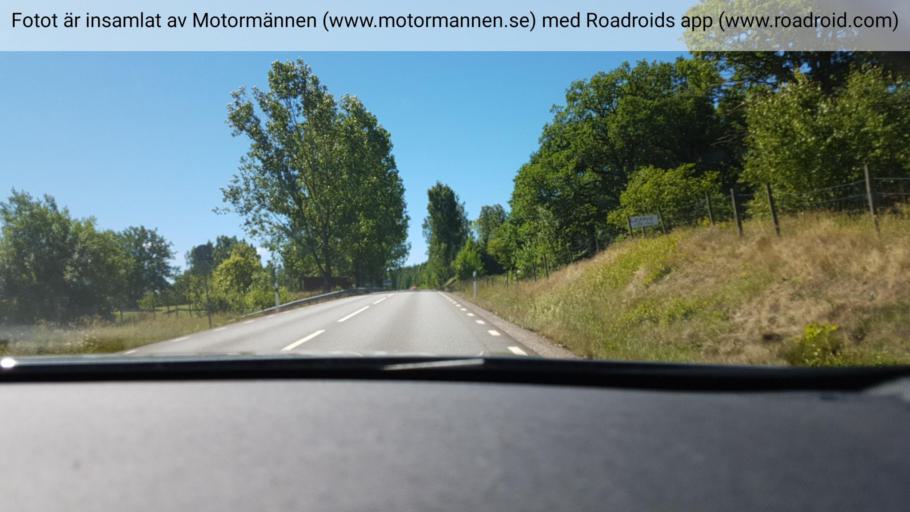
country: SE
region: Joenkoeping
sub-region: Mullsjo Kommun
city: Mullsjoe
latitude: 57.8382
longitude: 13.8531
